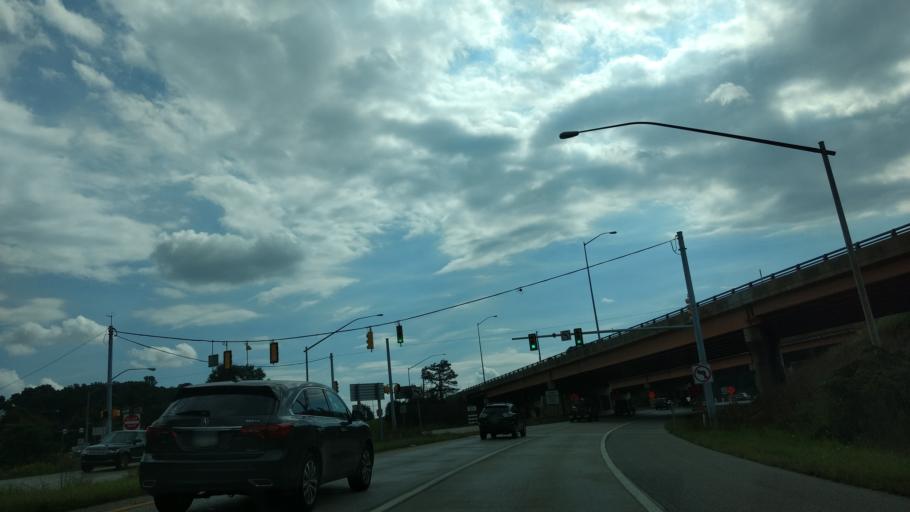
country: US
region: Pennsylvania
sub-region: Allegheny County
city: Bradford Woods
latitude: 40.6507
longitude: -80.0938
